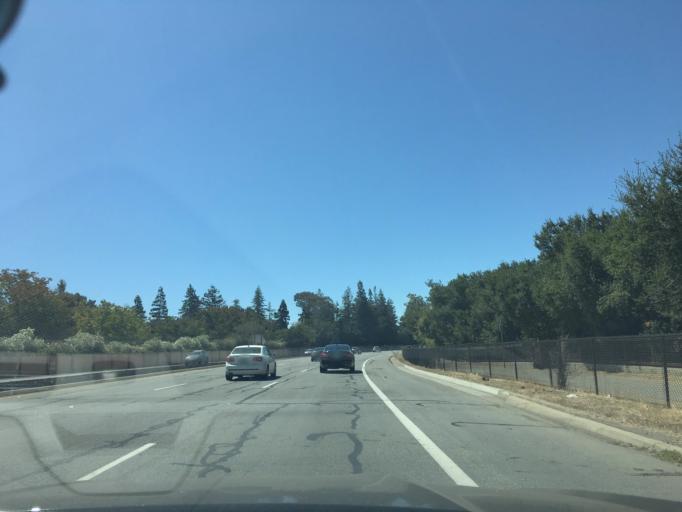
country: US
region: California
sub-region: Santa Clara County
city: Cupertino
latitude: 37.3047
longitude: -121.9962
